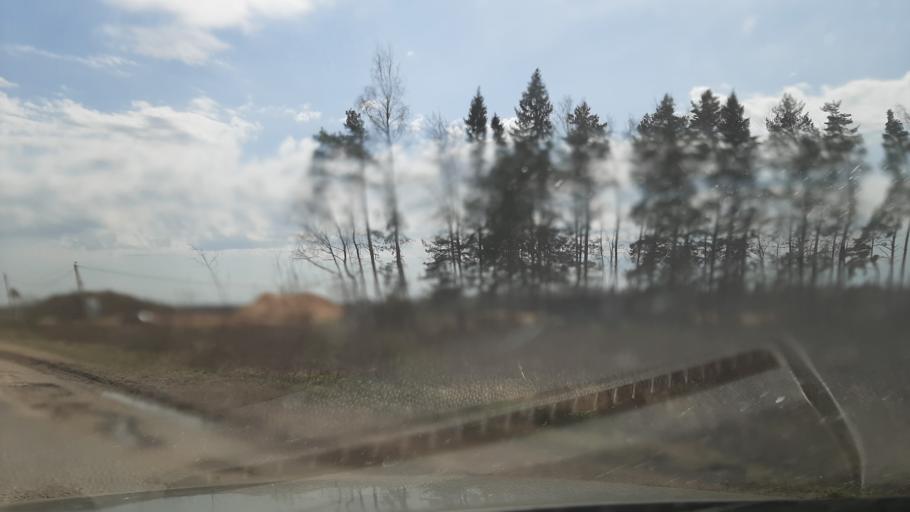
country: RU
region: Ivanovo
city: Furmanov
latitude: 57.1719
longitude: 41.0625
